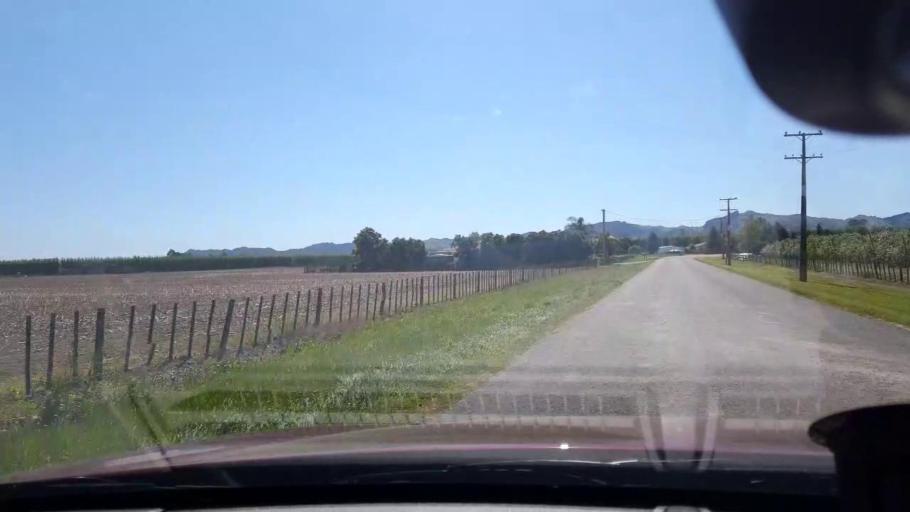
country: NZ
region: Gisborne
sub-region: Gisborne District
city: Gisborne
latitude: -38.6379
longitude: 177.9399
